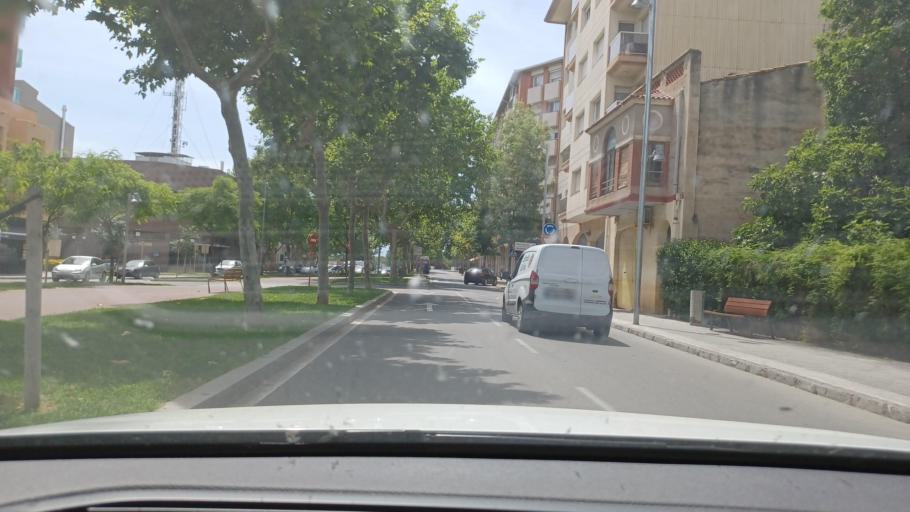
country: ES
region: Catalonia
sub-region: Provincia de Tarragona
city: Cambrils
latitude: 41.0717
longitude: 1.0533
